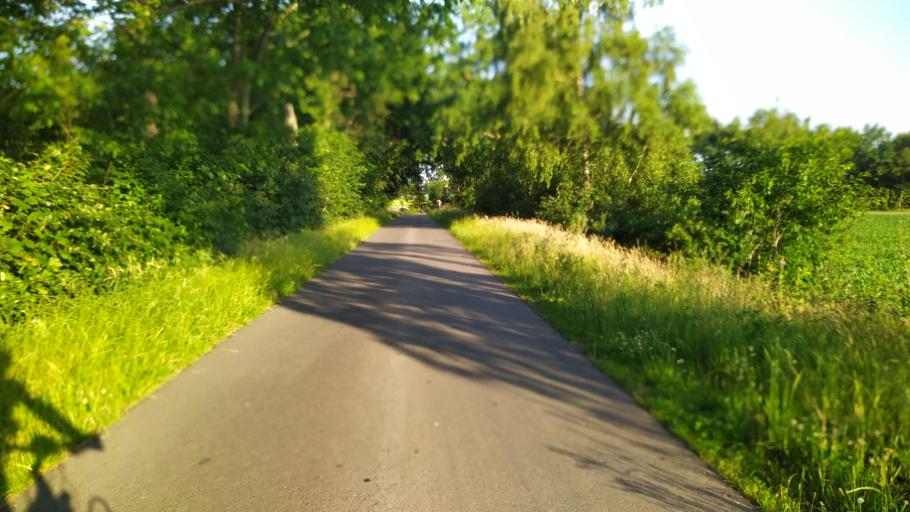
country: DE
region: Lower Saxony
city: Alfstedt
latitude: 53.5655
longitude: 9.0295
